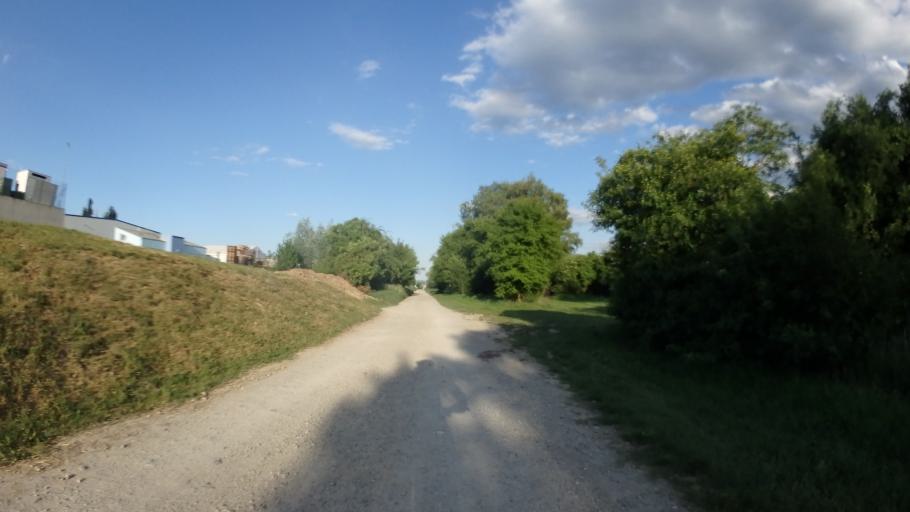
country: CZ
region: South Moravian
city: Moravany
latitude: 49.1442
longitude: 16.5858
